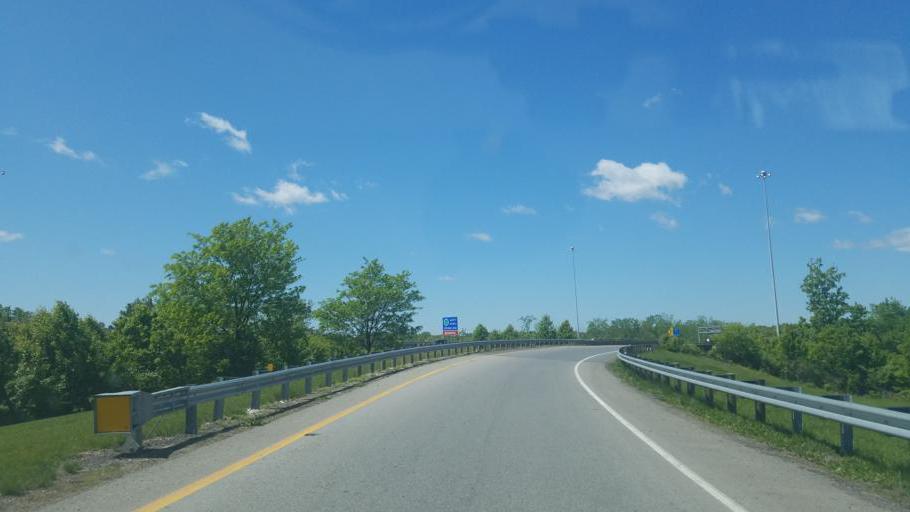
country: US
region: Ohio
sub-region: Franklin County
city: Huber Ridge
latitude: 40.1020
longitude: -82.9269
